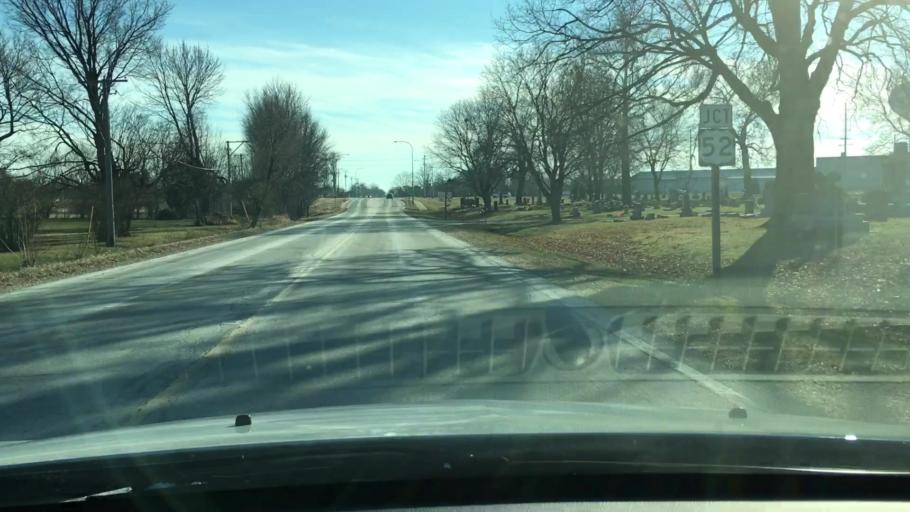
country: US
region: Illinois
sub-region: LaSalle County
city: Mendota
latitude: 41.5642
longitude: -89.1280
